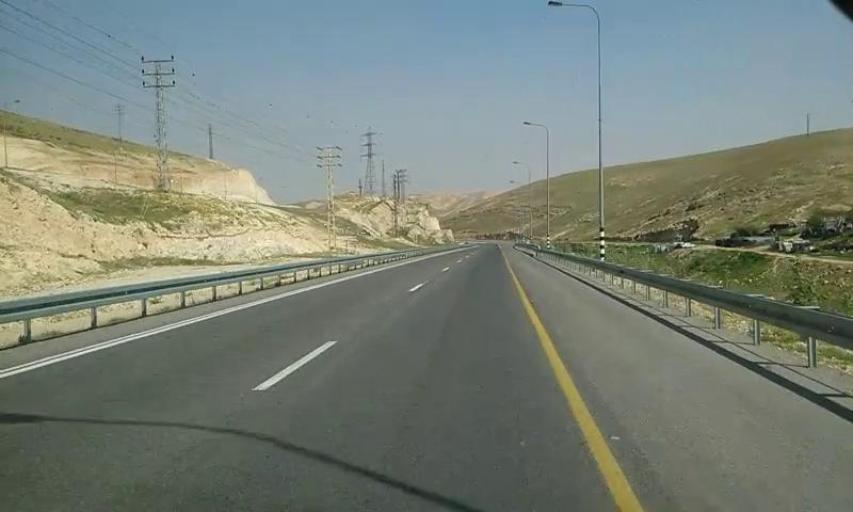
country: PS
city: Az Za`ayyim
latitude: 31.8087
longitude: 35.3350
